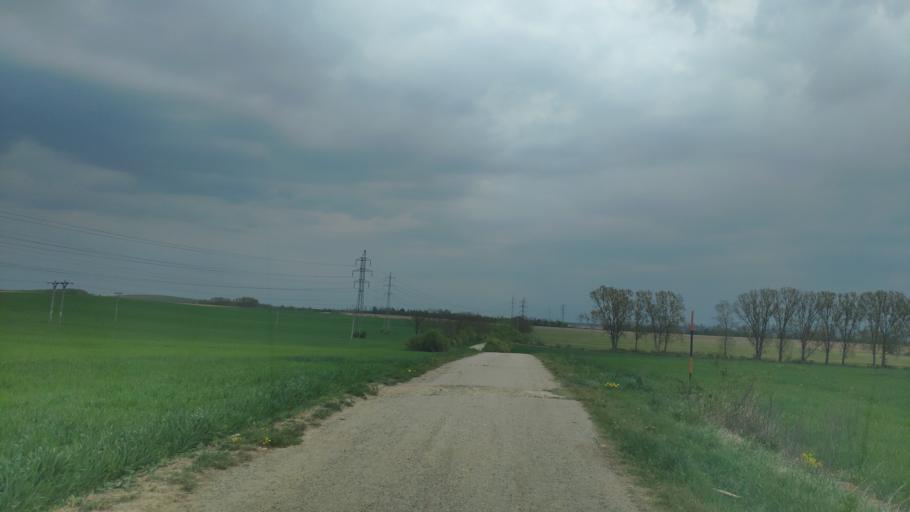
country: SK
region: Kosicky
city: Moldava nad Bodvou
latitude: 48.6030
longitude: 21.0268
